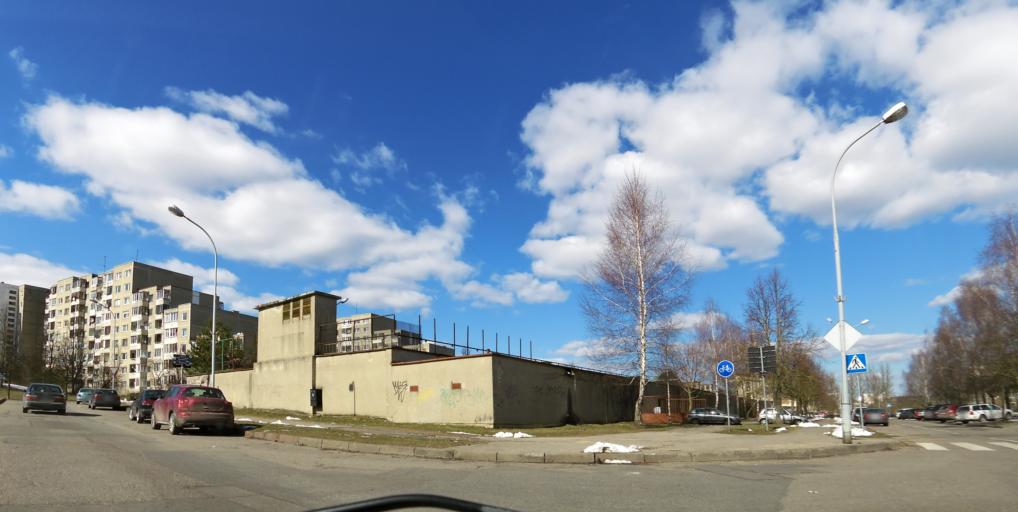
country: LT
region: Vilnius County
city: Pasilaiciai
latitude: 54.7258
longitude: 25.2263
